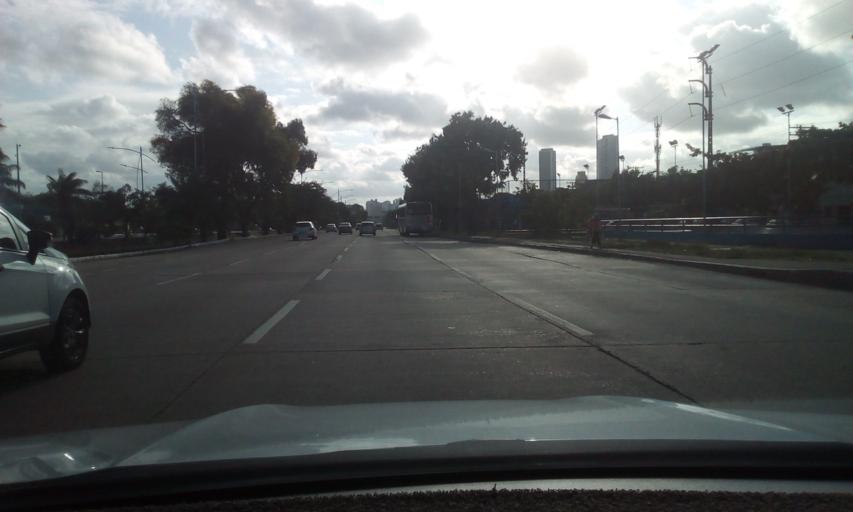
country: BR
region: Pernambuco
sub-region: Recife
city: Recife
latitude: -8.0376
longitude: -34.8747
